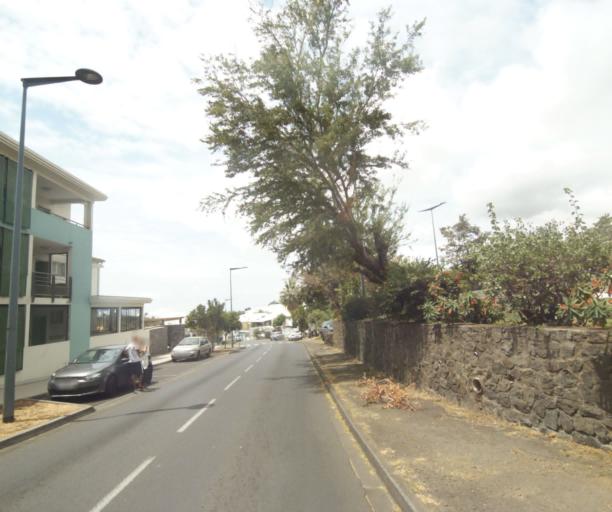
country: RE
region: Reunion
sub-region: Reunion
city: Saint-Paul
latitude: -21.0258
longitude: 55.2657
